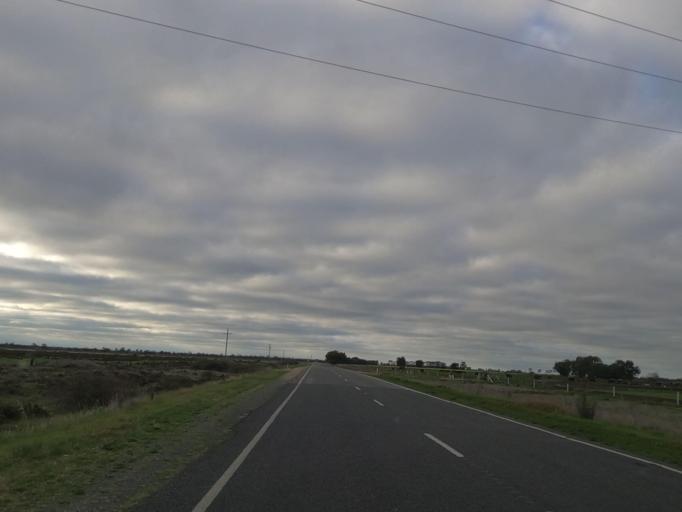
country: AU
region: Victoria
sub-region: Swan Hill
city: Swan Hill
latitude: -35.8349
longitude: 143.9423
